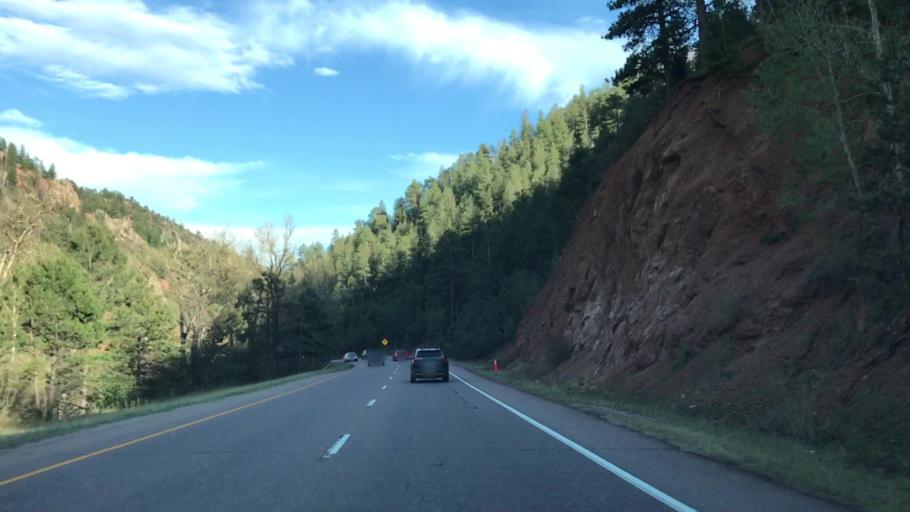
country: US
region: Colorado
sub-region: El Paso County
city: Manitou Springs
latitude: 38.8887
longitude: -104.9574
